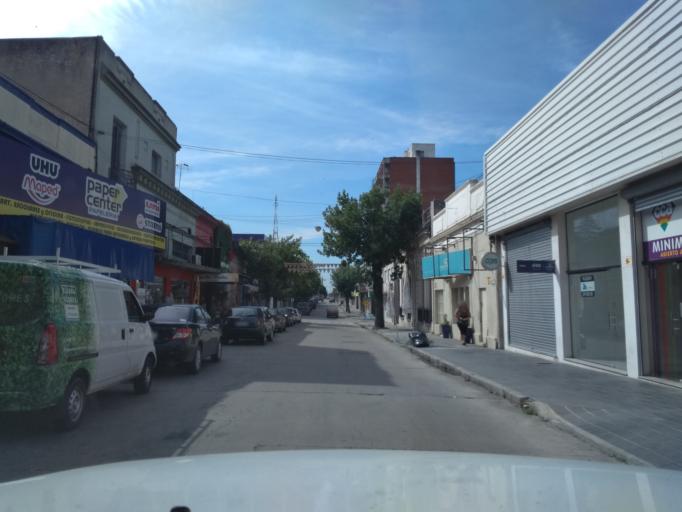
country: UY
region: Florida
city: Florida
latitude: -34.0953
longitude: -56.2191
